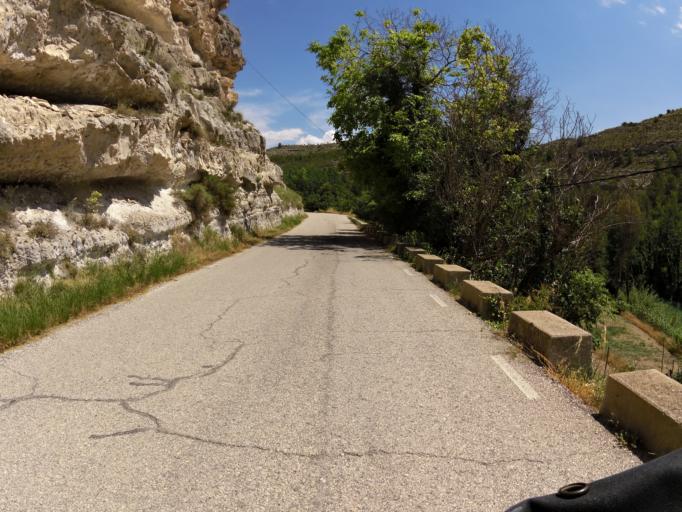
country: ES
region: Castille-La Mancha
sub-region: Provincia de Albacete
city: Jorquera
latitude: 39.1763
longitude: -1.5279
